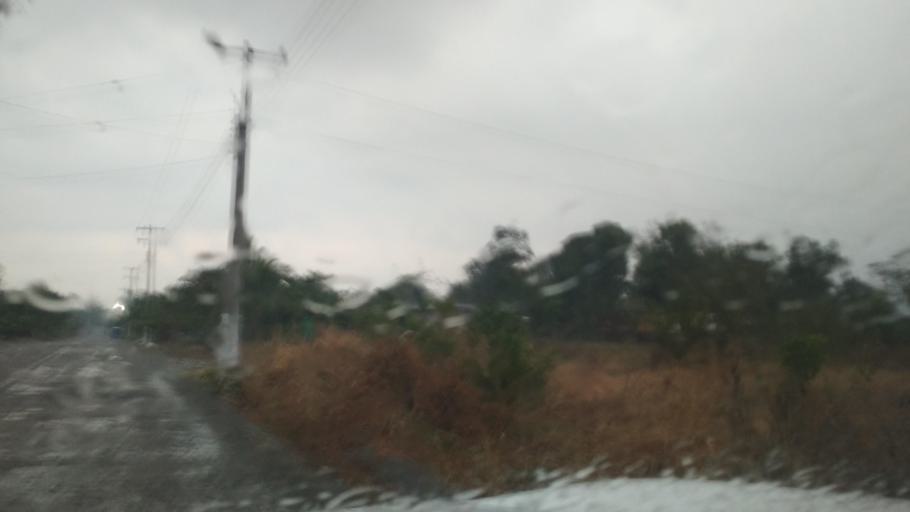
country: MM
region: Shan
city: Taunggyi
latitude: 20.3022
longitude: 97.3051
